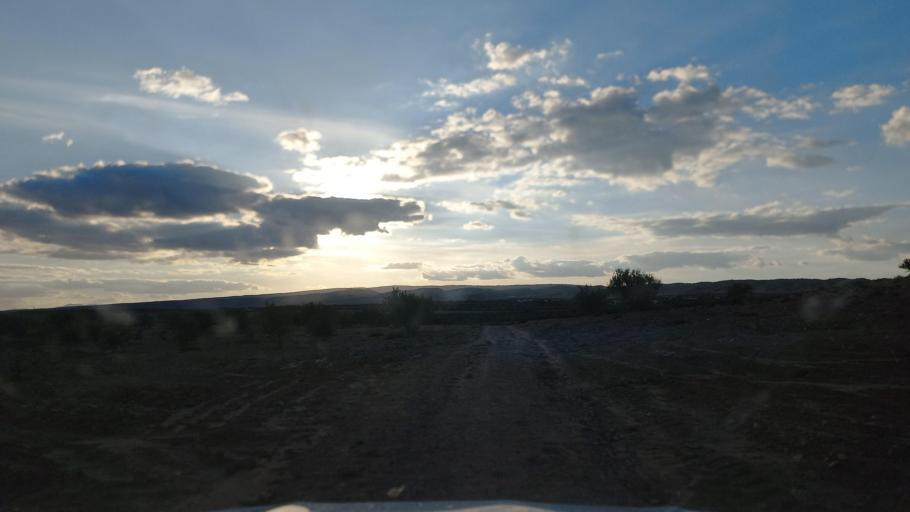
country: TN
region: Al Qasrayn
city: Sbiba
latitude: 35.3532
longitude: 9.0282
